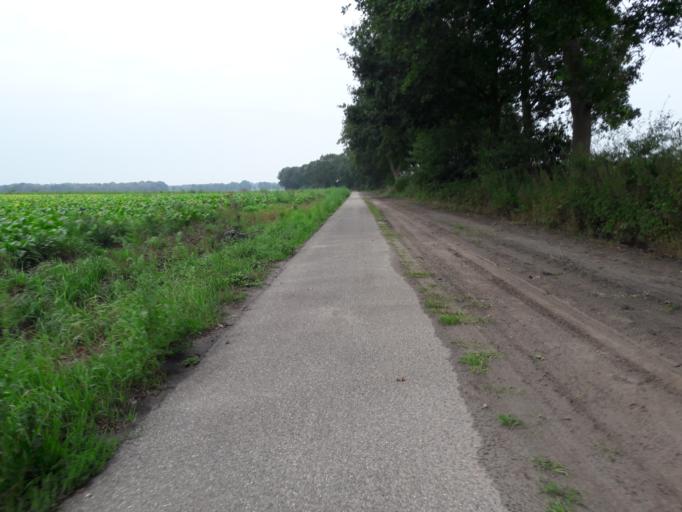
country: NL
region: Drenthe
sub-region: Gemeente Borger-Odoorn
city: Borger
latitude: 52.9369
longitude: 6.8190
